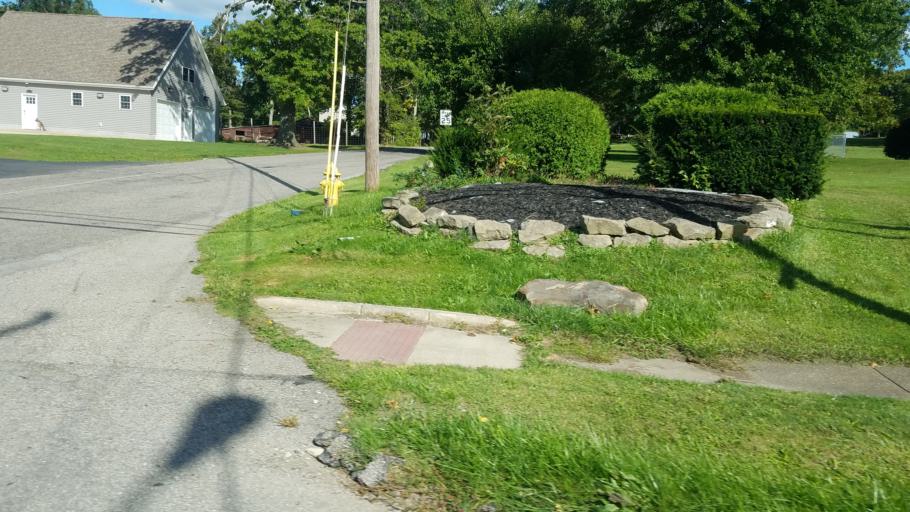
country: US
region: Ohio
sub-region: Trumbull County
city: Mineral Ridge
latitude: 41.1517
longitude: -80.7688
